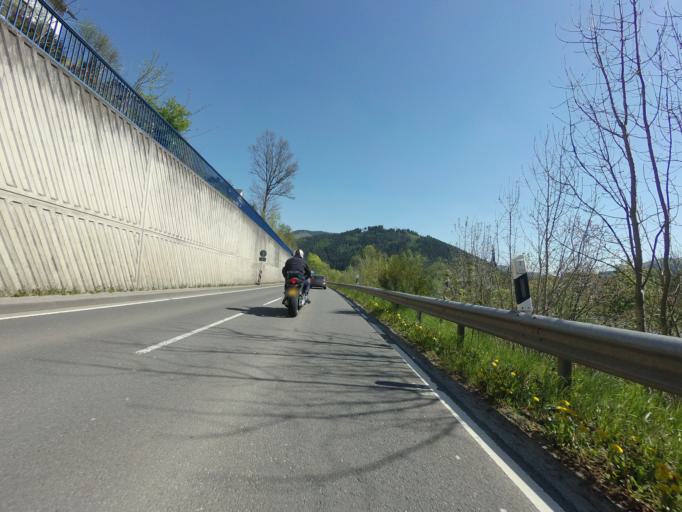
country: DE
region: North Rhine-Westphalia
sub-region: Regierungsbezirk Arnsberg
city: Lennestadt
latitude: 51.1031
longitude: 8.0694
